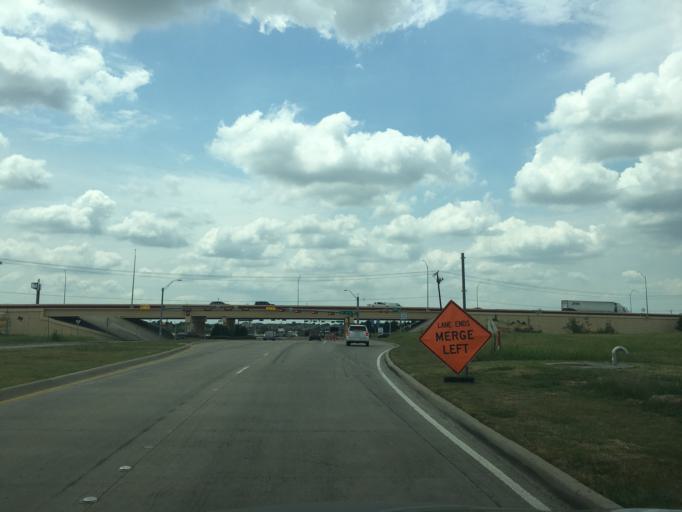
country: US
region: Texas
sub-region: Rockwall County
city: Rockwall
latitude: 32.9176
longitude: -96.4330
